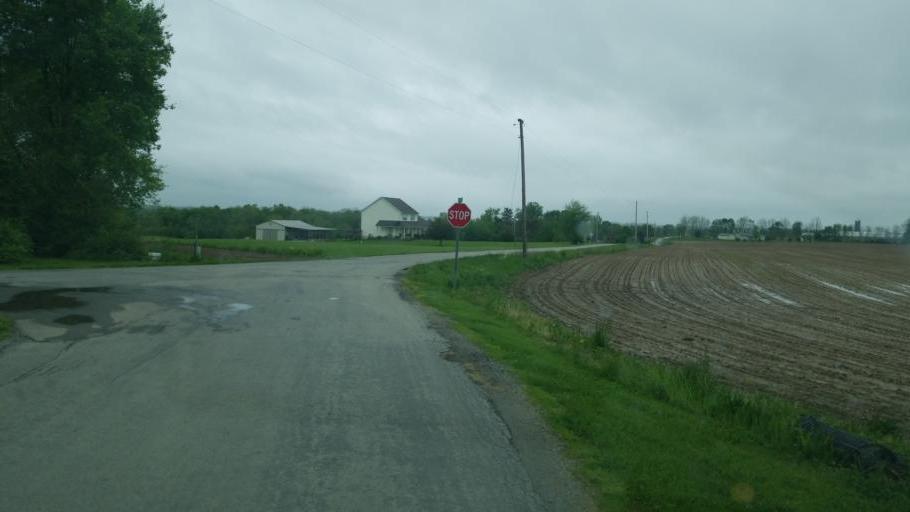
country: US
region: Ohio
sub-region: Highland County
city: Leesburg
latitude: 39.3312
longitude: -83.5001
